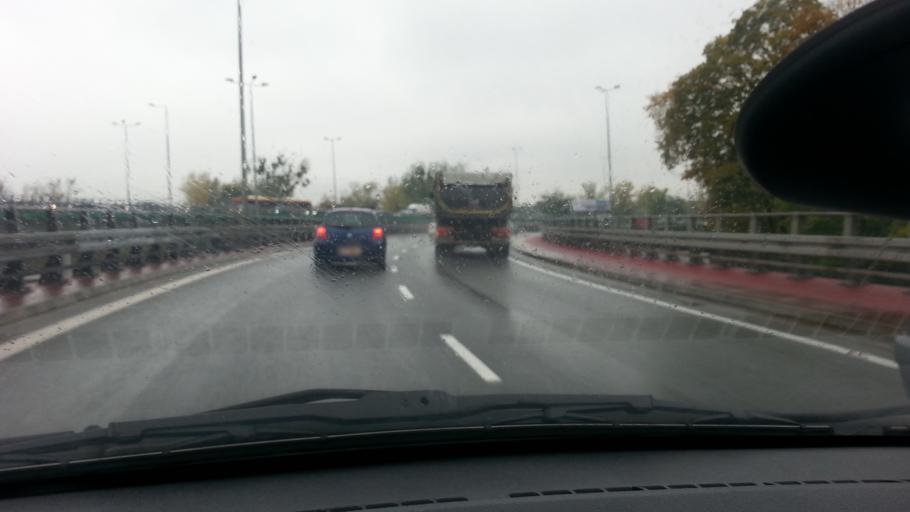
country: PL
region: Masovian Voivodeship
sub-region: Warszawa
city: Bielany
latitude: 52.2560
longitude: 20.9490
